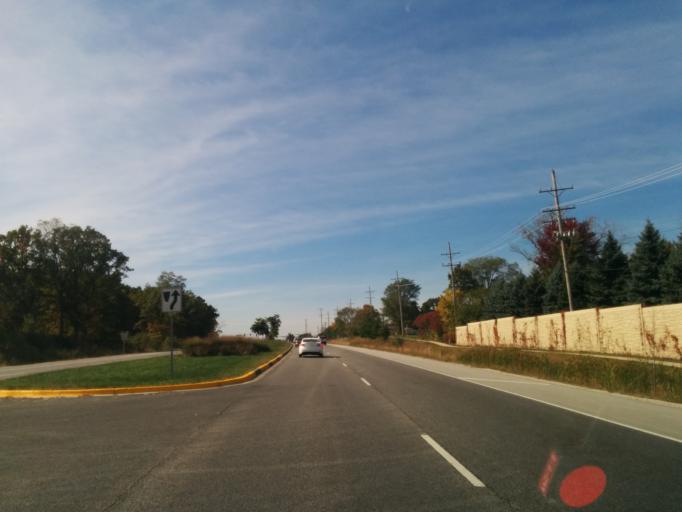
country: US
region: Illinois
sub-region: DuPage County
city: Warrenville
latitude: 41.8312
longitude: -88.1427
